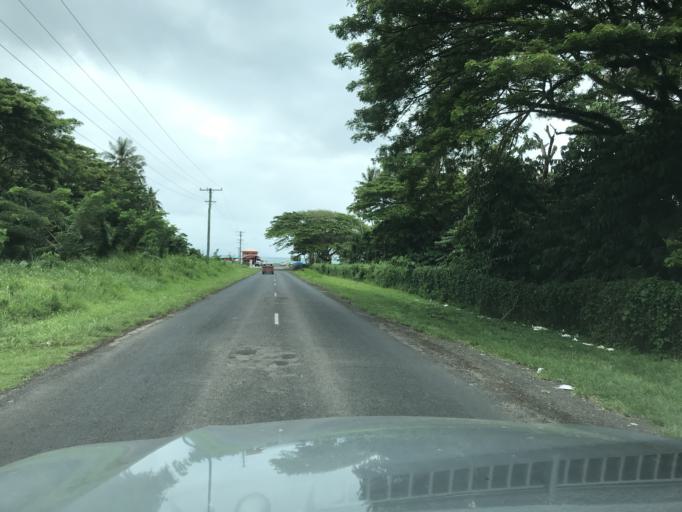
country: WS
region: Aiga-i-le-Tai
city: Mulifanua
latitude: -13.8312
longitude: -172.0332
